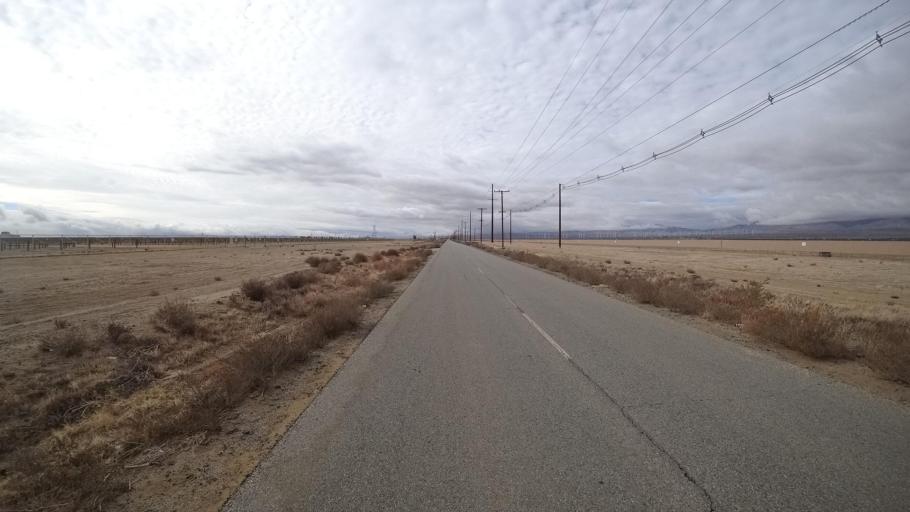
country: US
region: California
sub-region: Kern County
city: Rosamond
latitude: 34.8634
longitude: -118.3463
